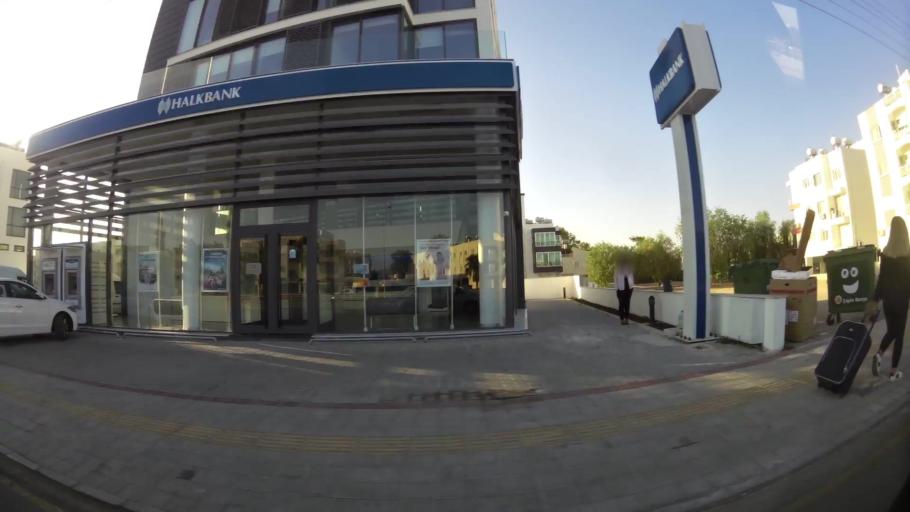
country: CY
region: Lefkosia
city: Nicosia
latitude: 35.2080
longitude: 33.3083
